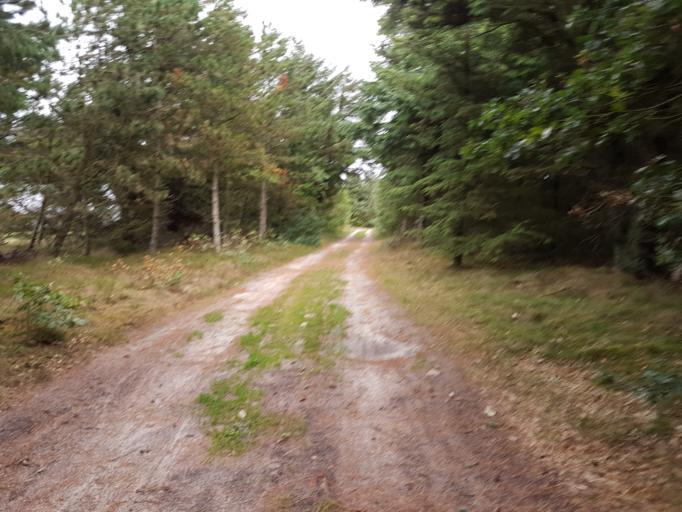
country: DK
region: Central Jutland
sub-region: Ringkobing-Skjern Kommune
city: Skjern
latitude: 55.8552
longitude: 8.2979
